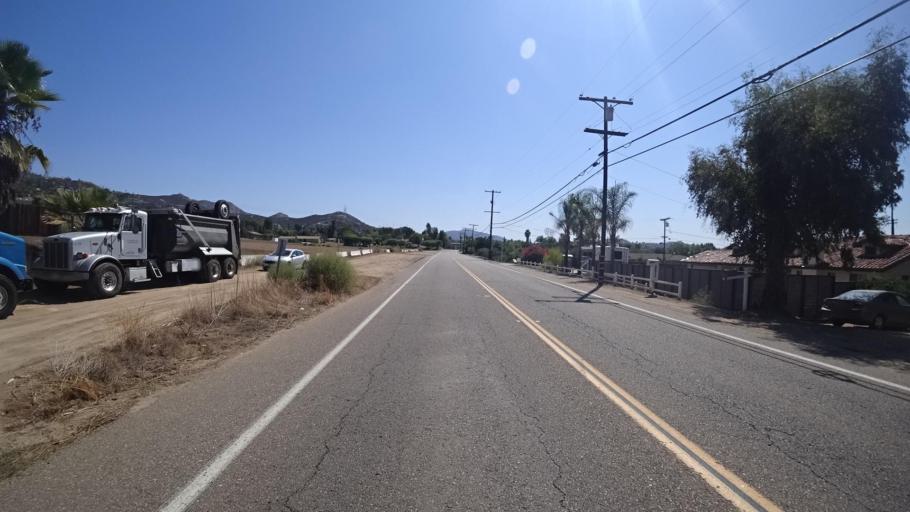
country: US
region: California
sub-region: San Diego County
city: Granite Hills
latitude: 32.8040
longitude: -116.9072
